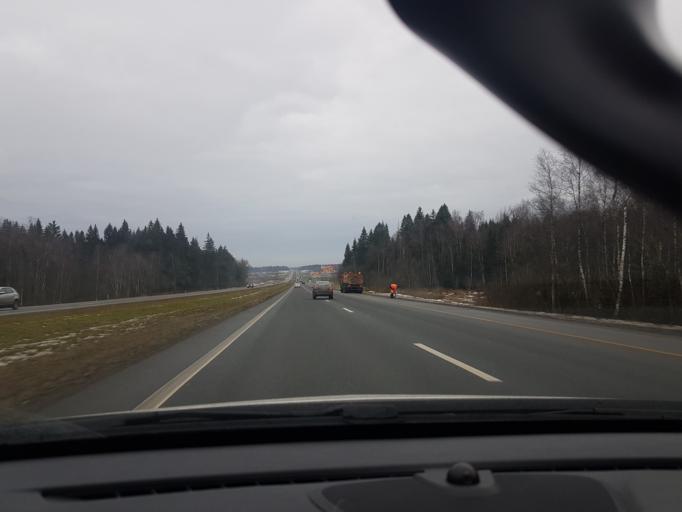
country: RU
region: Moskovskaya
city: Sychevo
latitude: 55.9918
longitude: 36.2535
